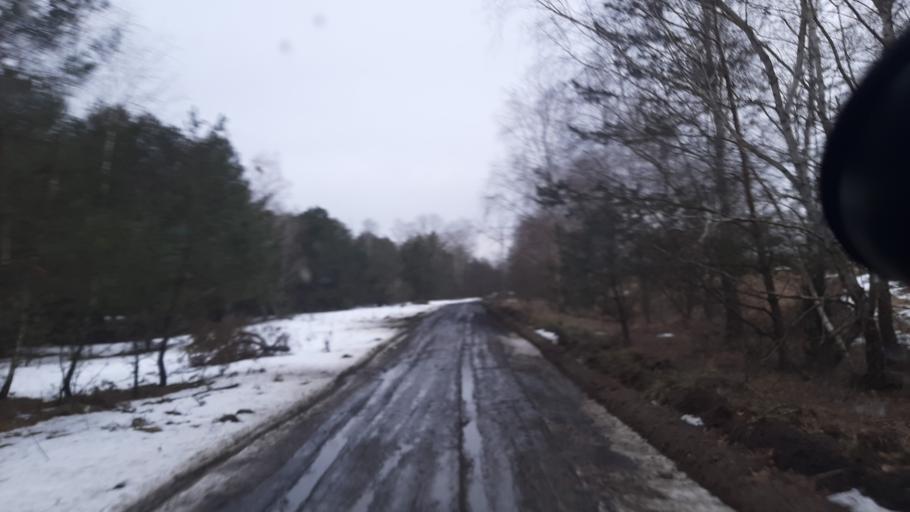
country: PL
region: Lublin Voivodeship
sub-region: Powiat wlodawski
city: Wlodawa
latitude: 51.5147
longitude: 23.6075
